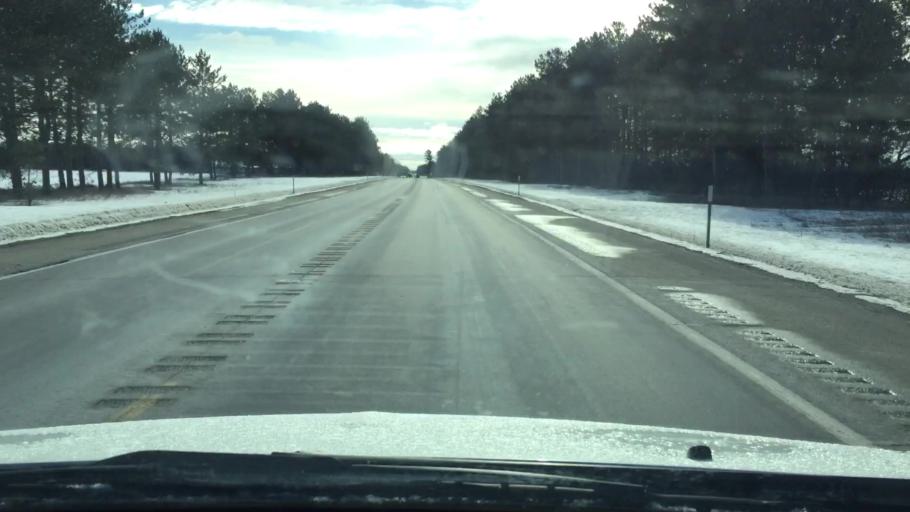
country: US
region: Michigan
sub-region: Antrim County
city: Mancelona
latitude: 44.8408
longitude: -85.1271
